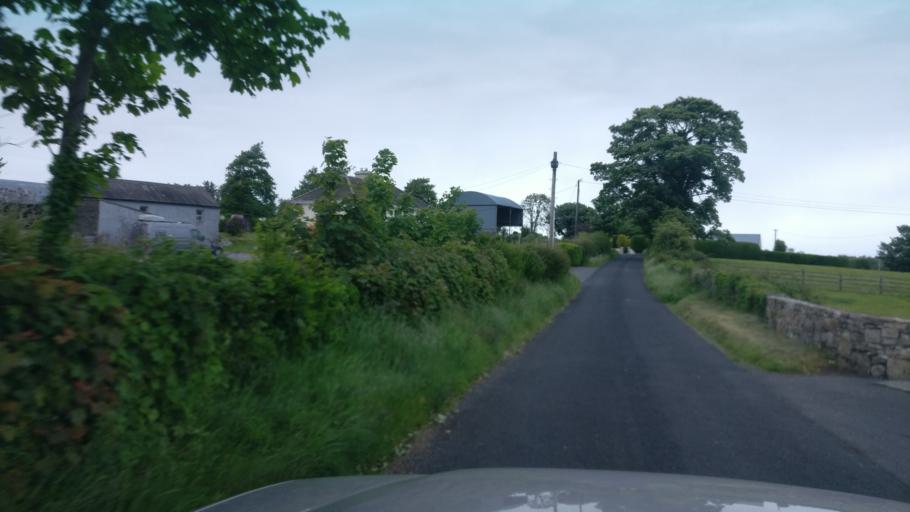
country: IE
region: Connaught
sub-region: County Galway
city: Loughrea
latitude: 53.1159
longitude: -8.4349
